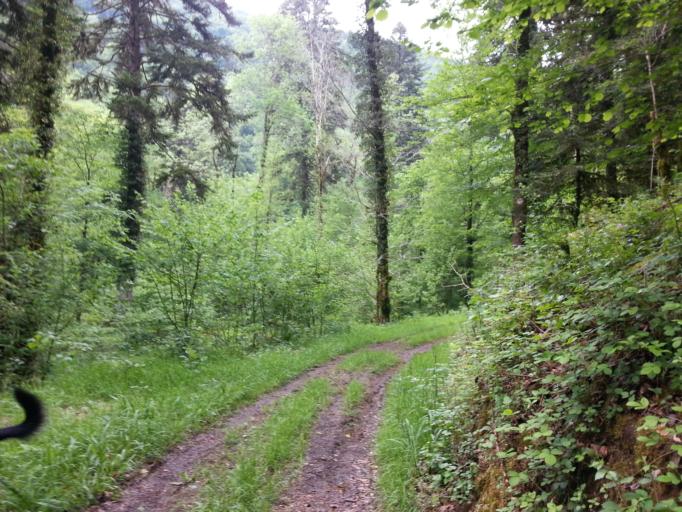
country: FR
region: Franche-Comte
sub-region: Departement du Jura
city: Salins-les-Bains
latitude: 47.0034
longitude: 5.9830
